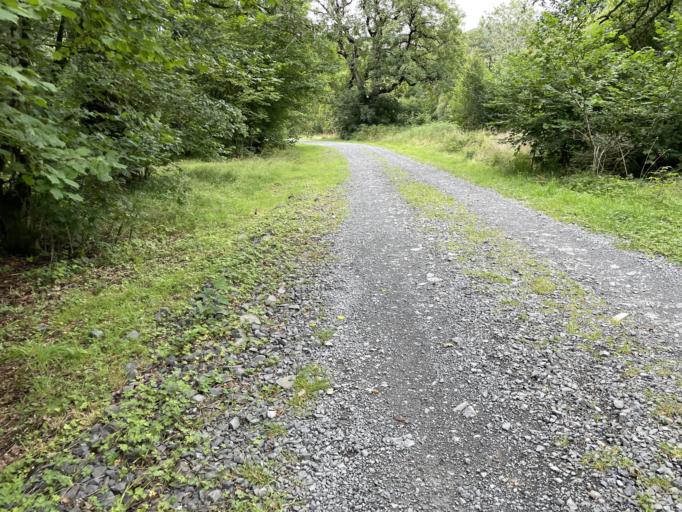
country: GB
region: Scotland
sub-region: Dumfries and Galloway
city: Newton Stewart
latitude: 55.0793
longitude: -4.5102
